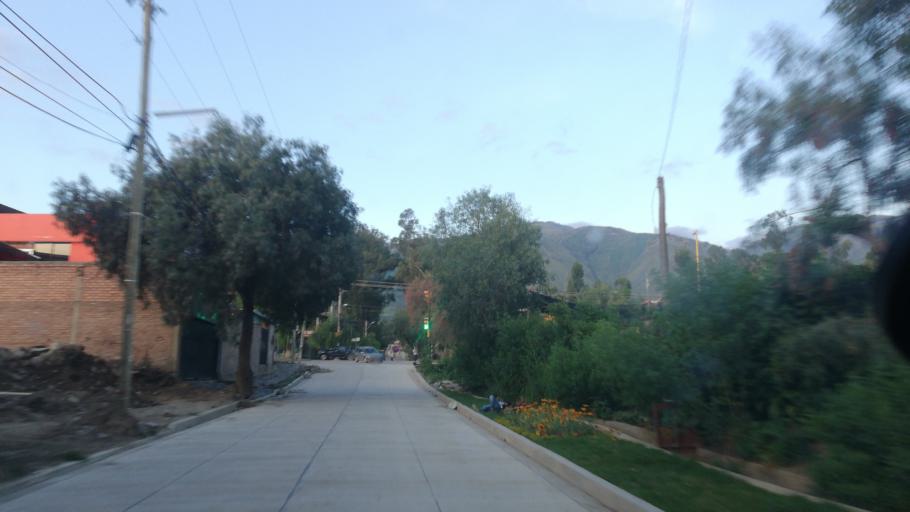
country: BO
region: Cochabamba
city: Cochabamba
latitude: -17.3431
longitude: -66.2112
